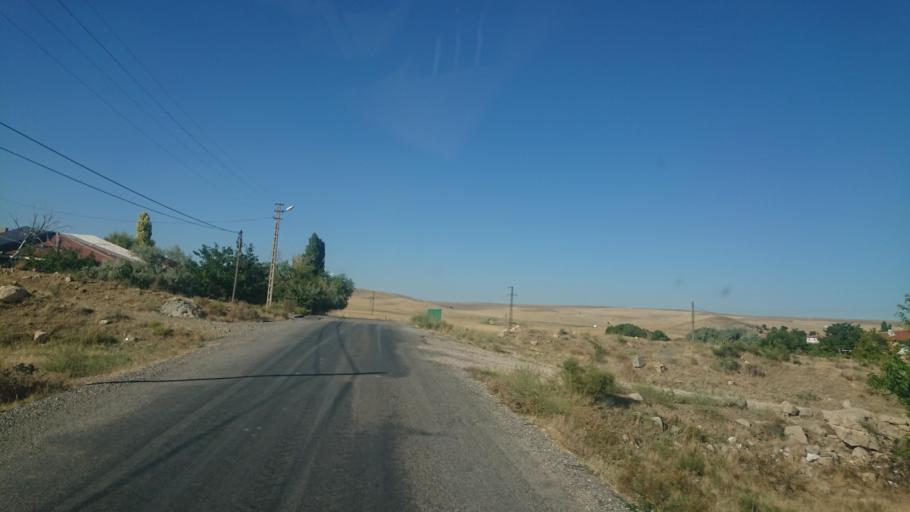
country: TR
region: Aksaray
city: Agacoren
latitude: 38.7727
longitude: 33.7061
